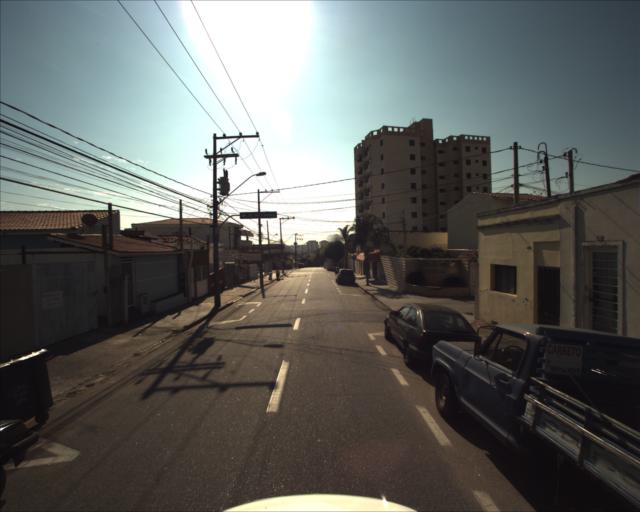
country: BR
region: Sao Paulo
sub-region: Sorocaba
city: Sorocaba
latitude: -23.4836
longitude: -47.4488
